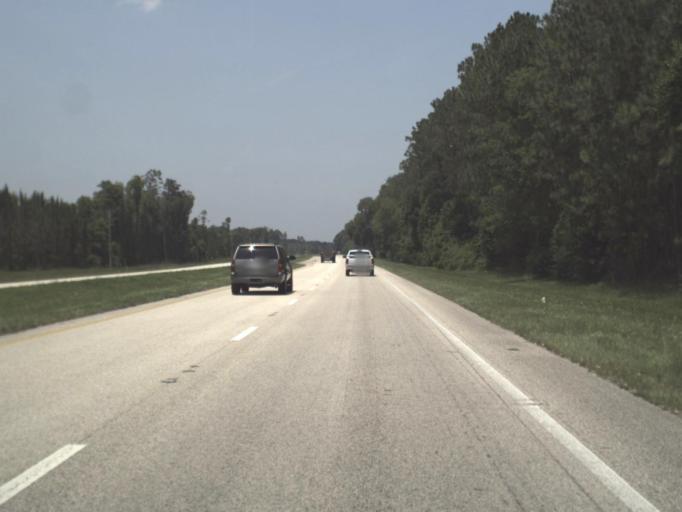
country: US
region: Florida
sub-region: Duval County
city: Baldwin
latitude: 30.1722
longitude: -82.0253
